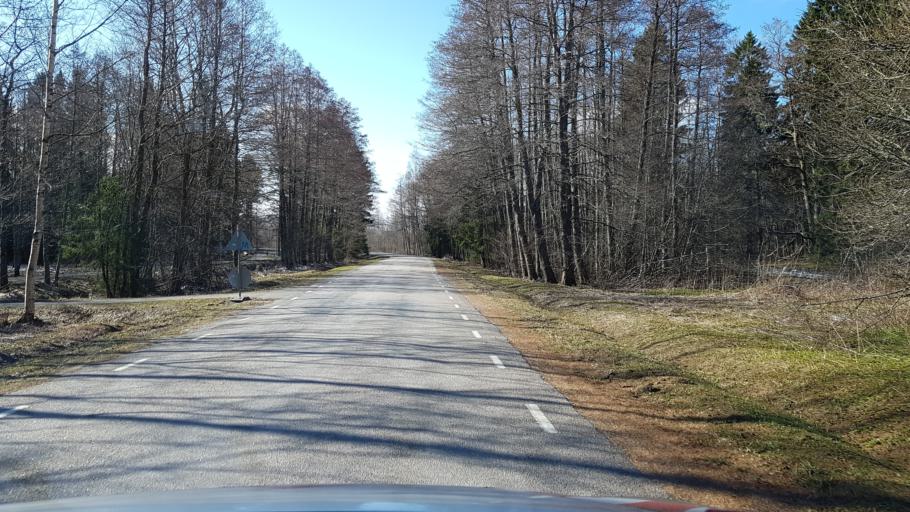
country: EE
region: Harju
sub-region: Loksa linn
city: Loksa
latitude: 59.5888
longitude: 25.9080
